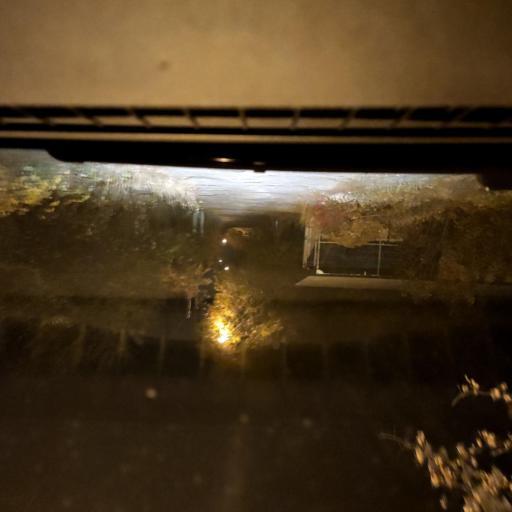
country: RU
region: Voronezj
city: Maslovka
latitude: 51.6192
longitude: 39.2608
